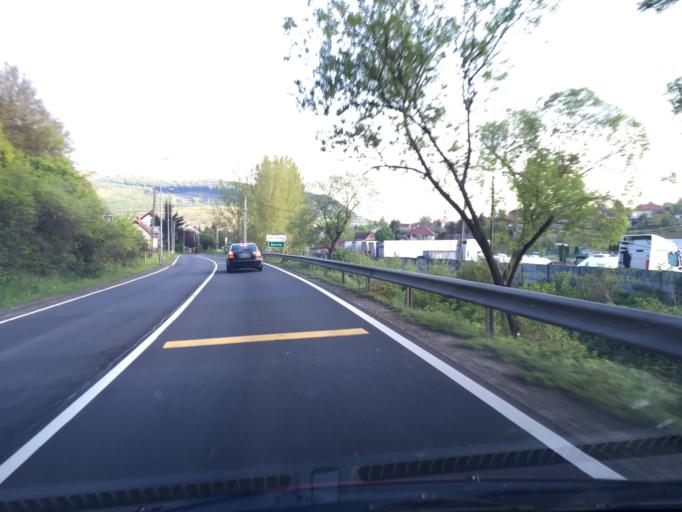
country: HU
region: Nograd
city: Retsag
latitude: 47.8609
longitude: 19.1058
